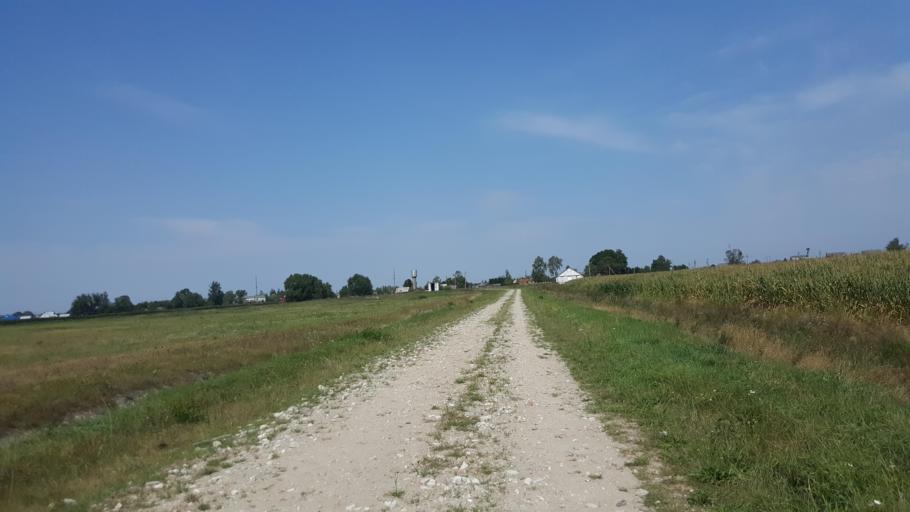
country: PL
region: Podlasie
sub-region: Powiat hajnowski
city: Czeremcha
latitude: 52.4896
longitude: 23.5728
